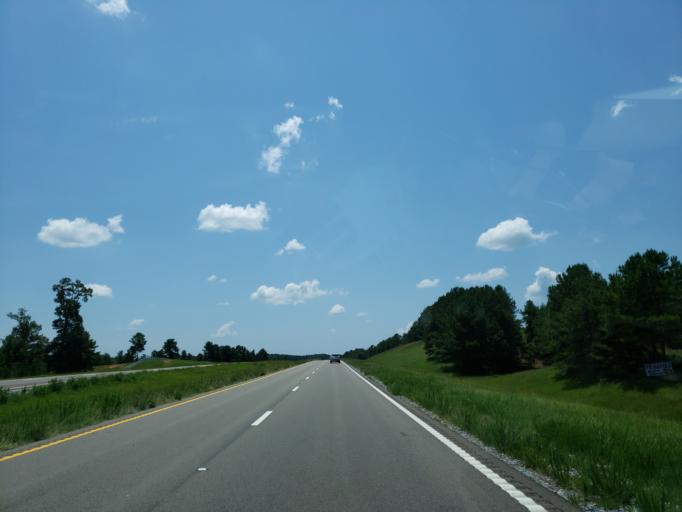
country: US
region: Mississippi
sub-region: Clarke County
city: Stonewall
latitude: 32.1252
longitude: -88.7151
